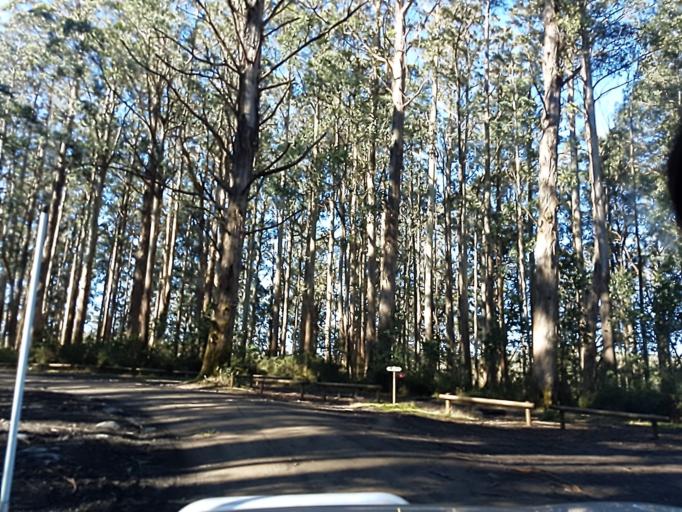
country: AU
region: Victoria
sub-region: Yarra Ranges
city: Healesville
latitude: -37.5593
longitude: 145.5272
